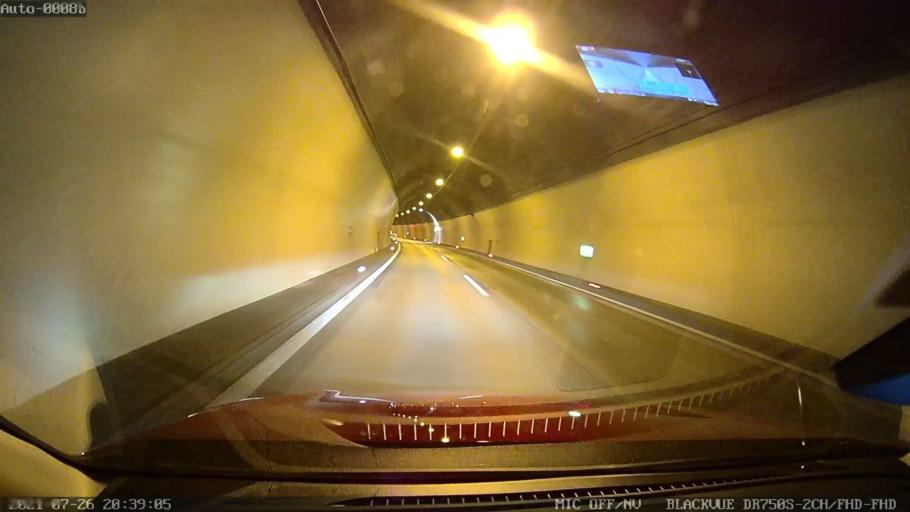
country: AT
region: Styria
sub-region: Politischer Bezirk Graz-Umgebung
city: Deutschfeistritz
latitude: 47.1953
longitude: 15.3265
